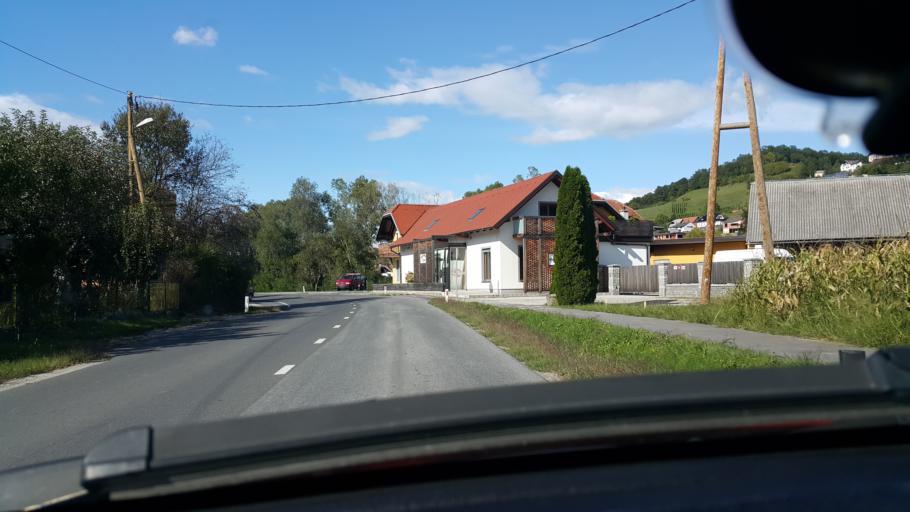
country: SI
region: Pesnica
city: Pesnica pri Mariboru
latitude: 46.6076
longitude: 15.6486
